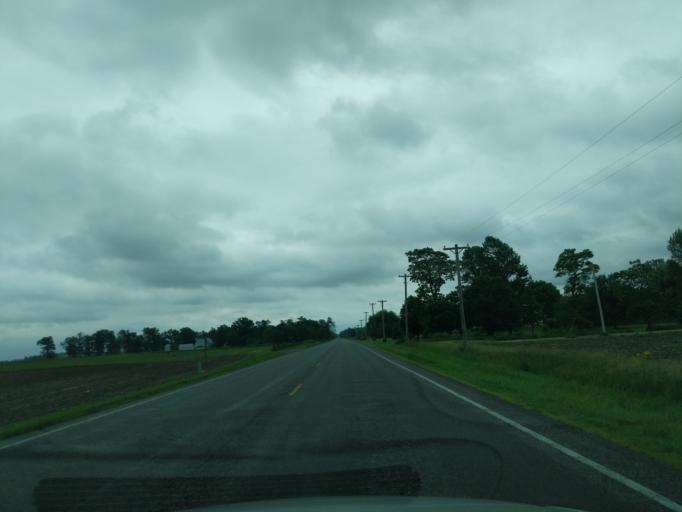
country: US
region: Indiana
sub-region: Tipton County
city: Tipton
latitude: 40.2833
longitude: -85.9862
